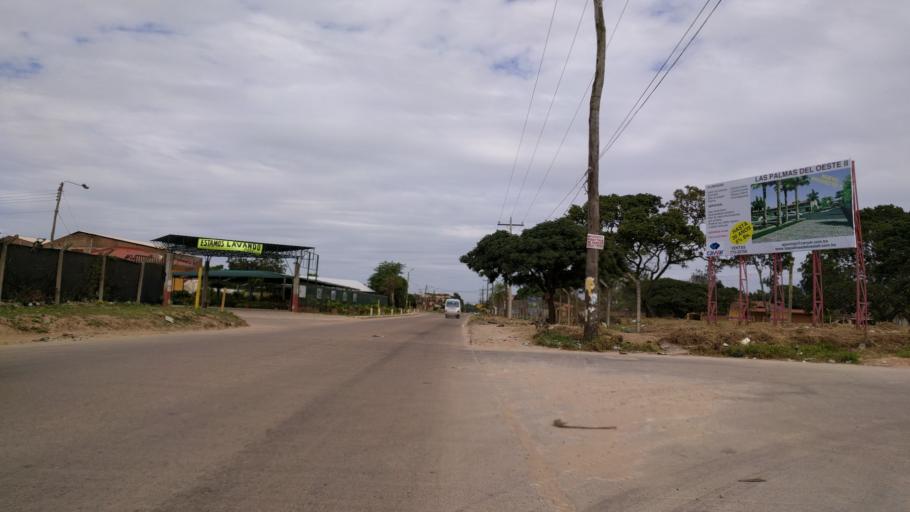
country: BO
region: Santa Cruz
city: Santa Cruz de la Sierra
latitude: -17.8190
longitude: -63.2332
